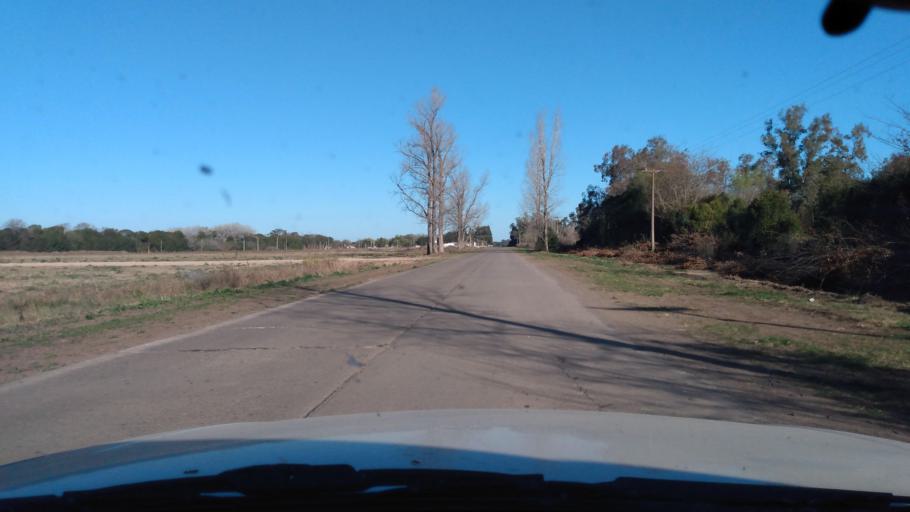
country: AR
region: Buenos Aires
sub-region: Partido de Mercedes
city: Mercedes
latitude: -34.6041
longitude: -59.2885
